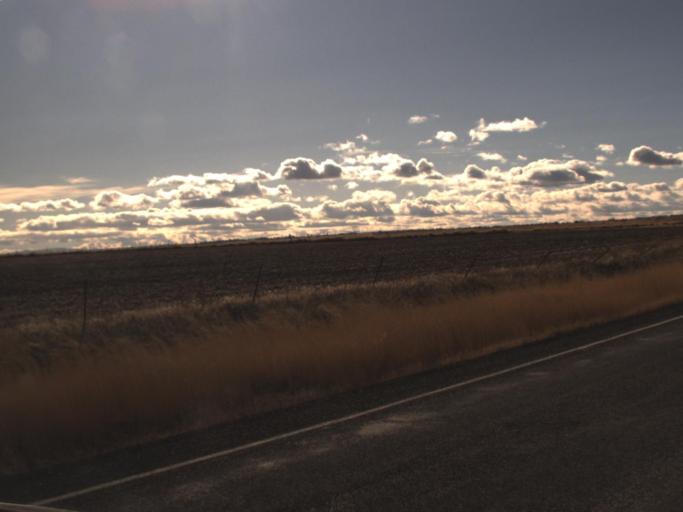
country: US
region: Washington
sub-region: Asotin County
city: Asotin
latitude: 46.1708
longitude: -117.0855
